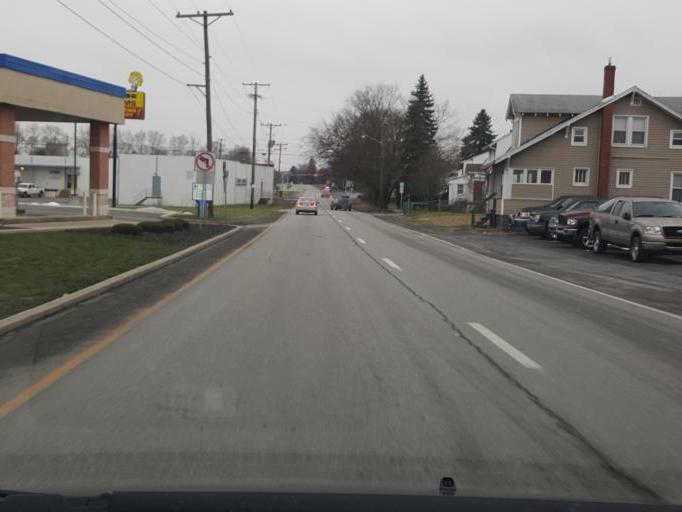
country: US
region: Pennsylvania
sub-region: Blair County
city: Altoona
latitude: 40.4990
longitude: -78.3924
